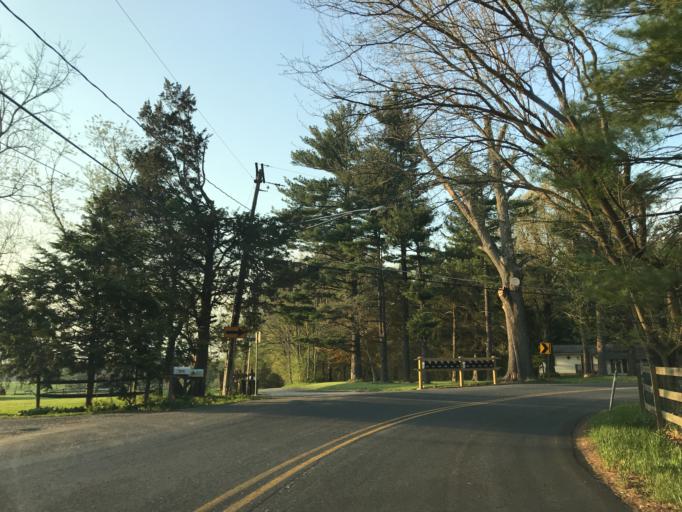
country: US
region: Maryland
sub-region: Harford County
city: Jarrettsville
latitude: 39.6216
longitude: -76.4838
